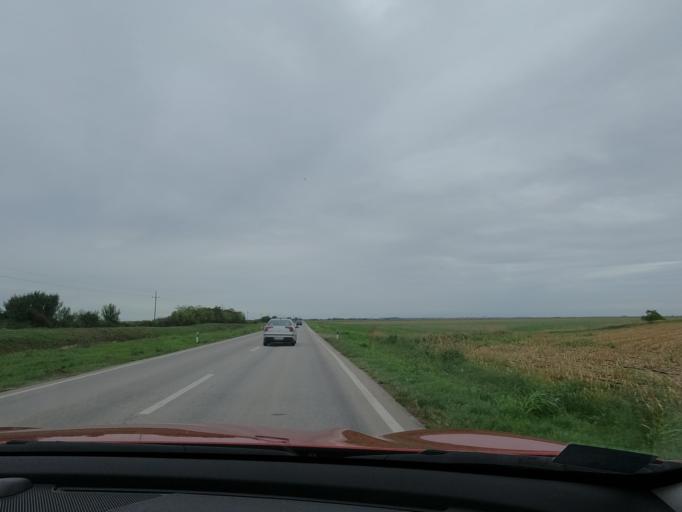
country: RS
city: Banatska Topola
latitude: 45.7483
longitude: 20.4215
